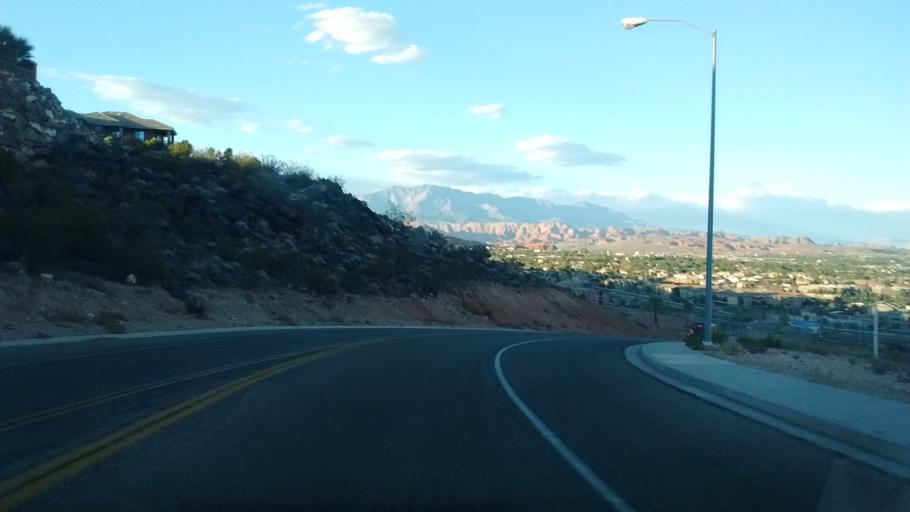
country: US
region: Utah
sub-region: Washington County
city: Saint George
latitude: 37.0952
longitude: -113.5444
